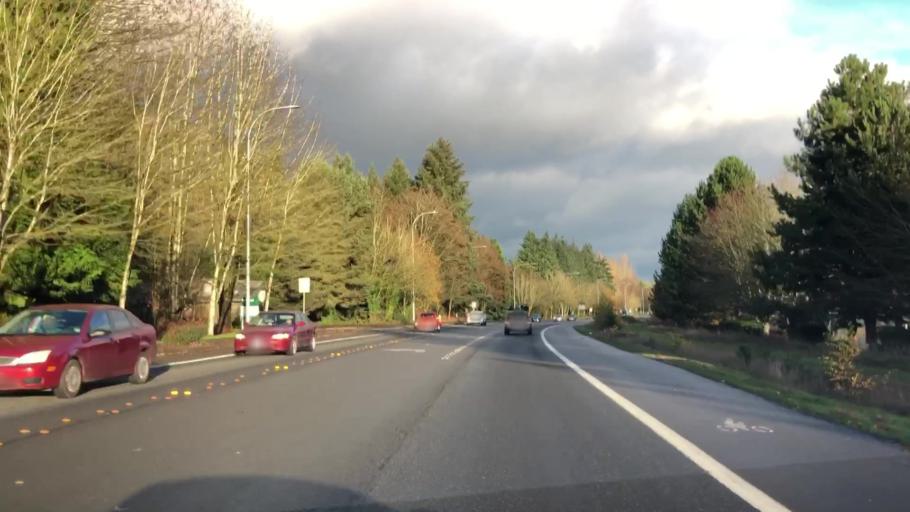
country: US
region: Washington
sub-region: King County
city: Redmond
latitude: 47.6901
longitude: -122.1500
